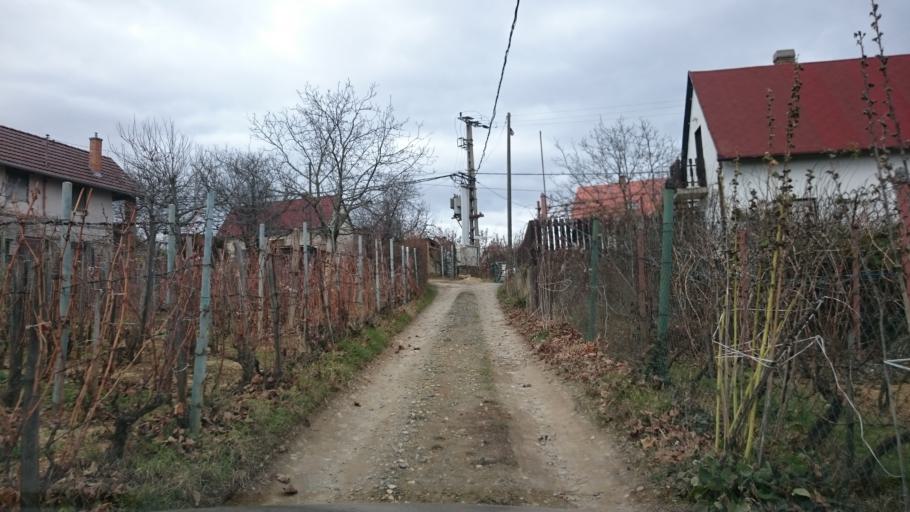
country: HU
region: Baranya
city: Pellerd
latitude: 46.0757
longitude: 18.1799
